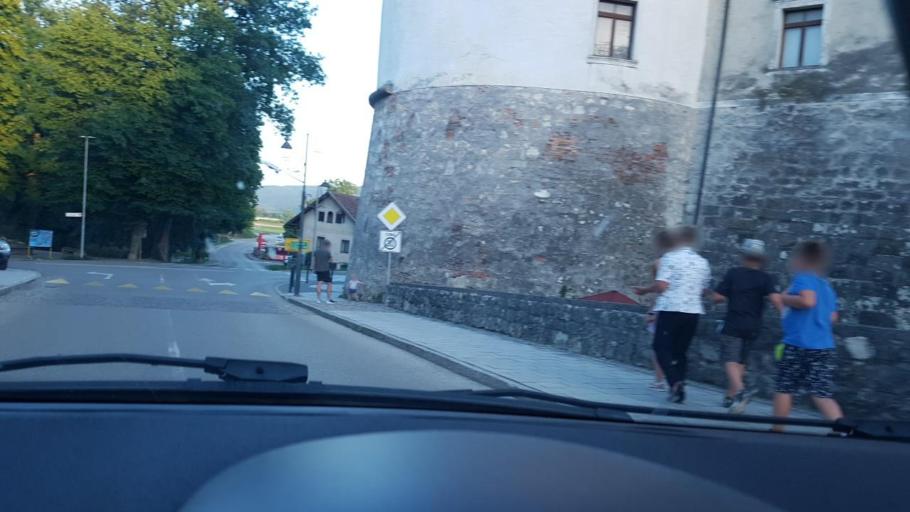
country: SI
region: Brezice
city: Brezice
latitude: 45.9021
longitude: 15.5928
